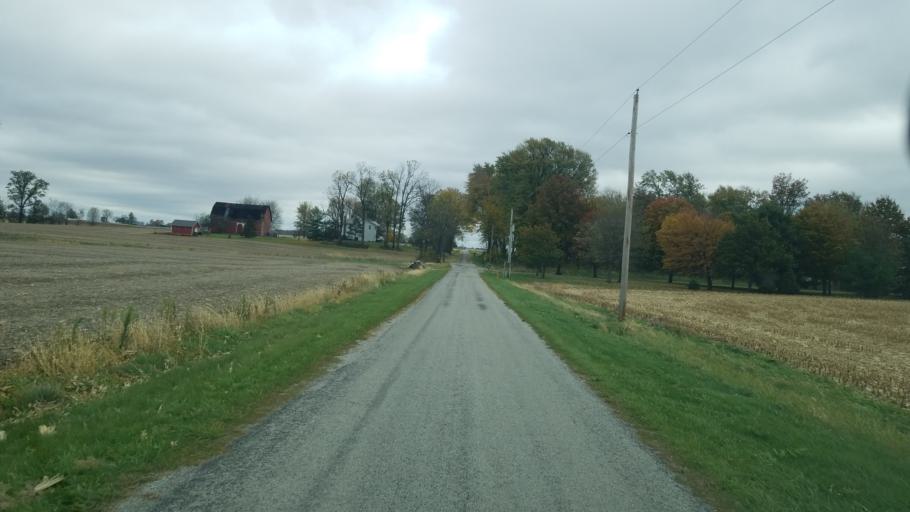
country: US
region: Ohio
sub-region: Crawford County
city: Bucyrus
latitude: 40.9072
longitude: -82.8673
